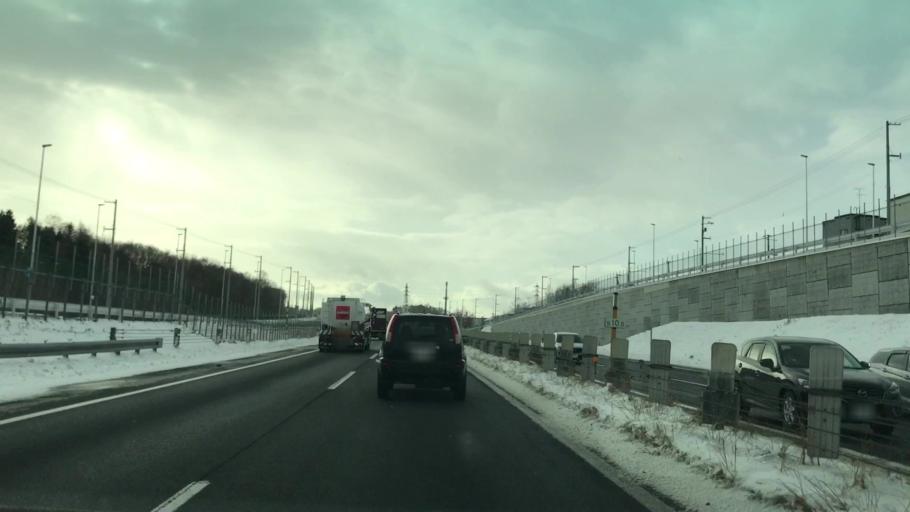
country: JP
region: Hokkaido
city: Kitahiroshima
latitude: 42.9912
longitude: 141.4696
